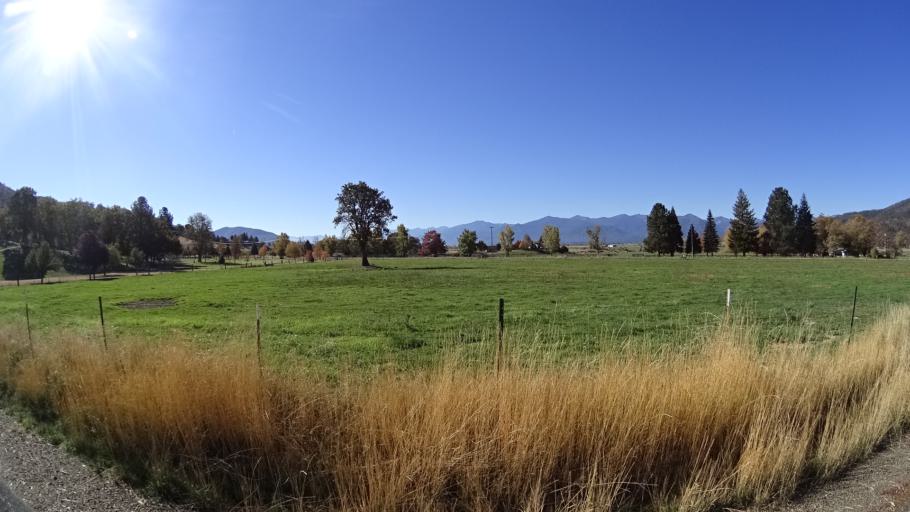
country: US
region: California
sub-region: Siskiyou County
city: Yreka
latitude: 41.5914
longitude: -122.8365
